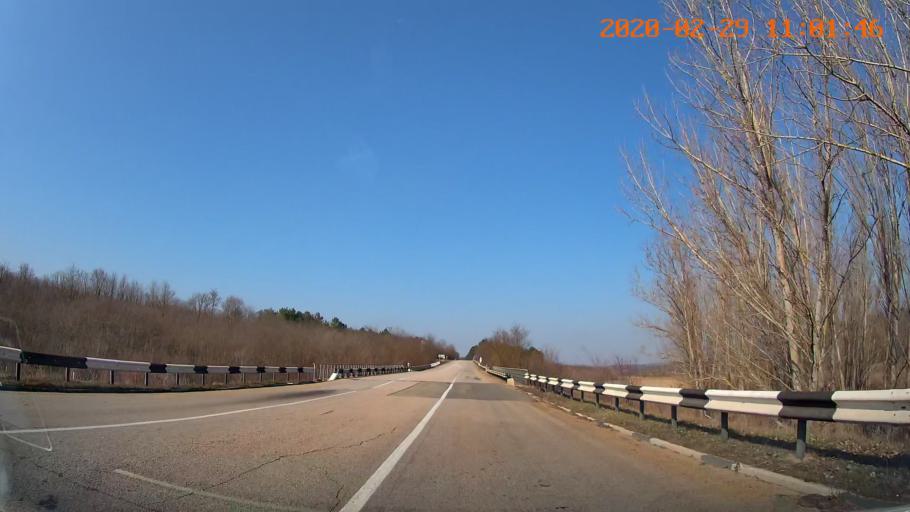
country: MD
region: Telenesti
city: Grigoriopol
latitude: 47.1669
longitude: 29.2515
